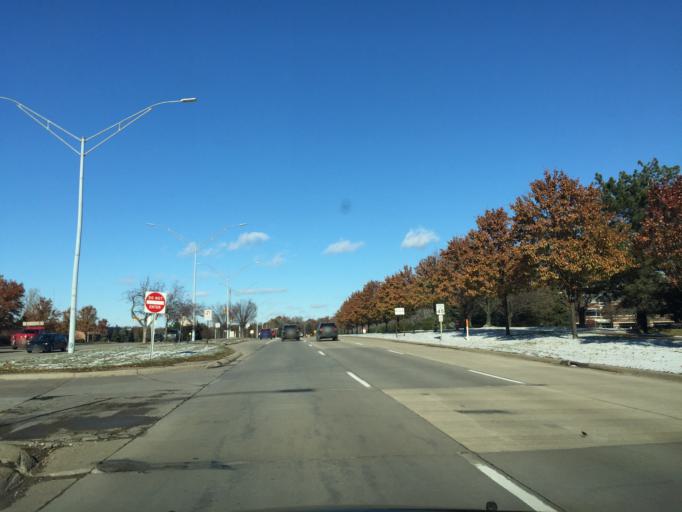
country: US
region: Michigan
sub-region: Oakland County
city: Auburn Hills
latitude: 42.6496
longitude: -83.2199
